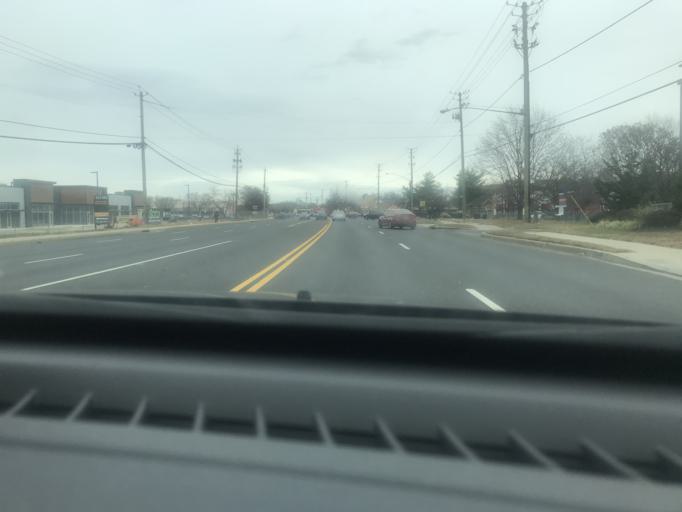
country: US
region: Maryland
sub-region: Prince George's County
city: Oxon Hill
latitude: 38.8045
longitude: -76.9790
